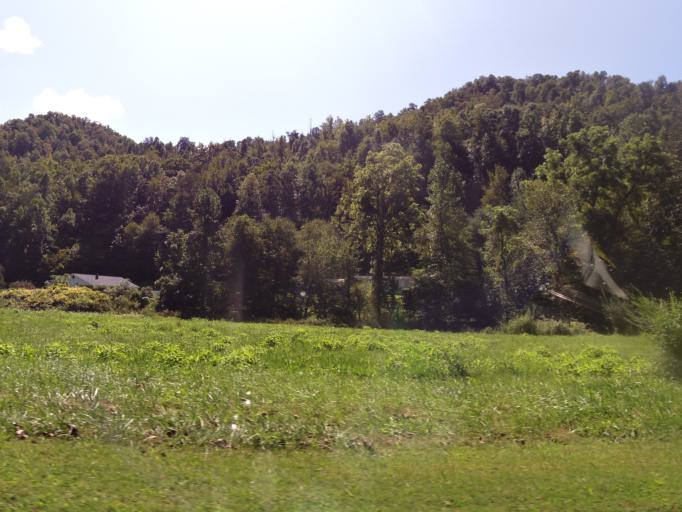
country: US
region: Kentucky
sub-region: Leslie County
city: Hyden
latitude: 37.1517
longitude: -83.3914
